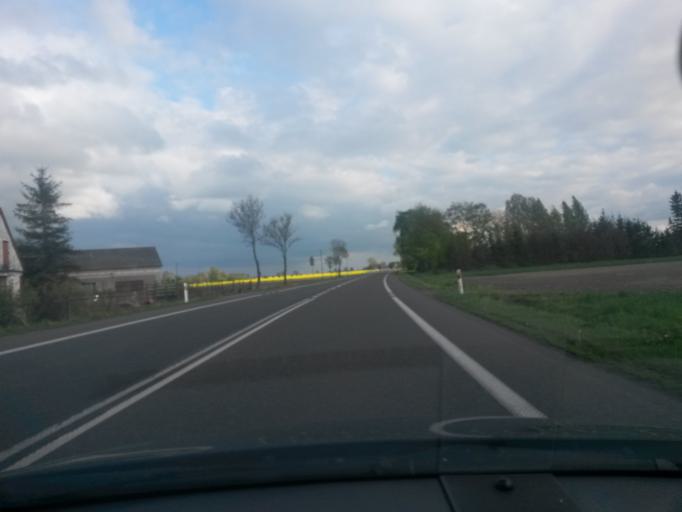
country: PL
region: Masovian Voivodeship
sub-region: Powiat plocki
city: Drobin
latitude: 52.7200
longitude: 20.0181
